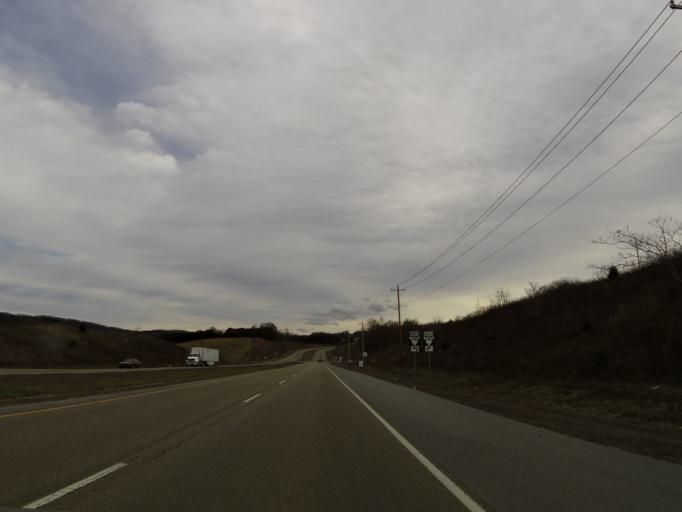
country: US
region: Tennessee
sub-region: Cocke County
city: Newport
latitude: 36.0037
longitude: -83.0939
